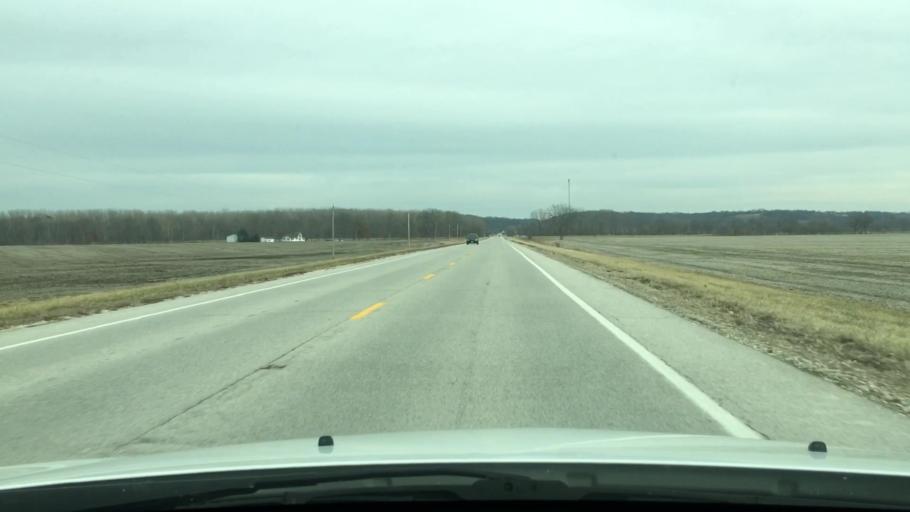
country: US
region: Missouri
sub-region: Pike County
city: Louisiana
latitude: 39.4997
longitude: -90.9981
